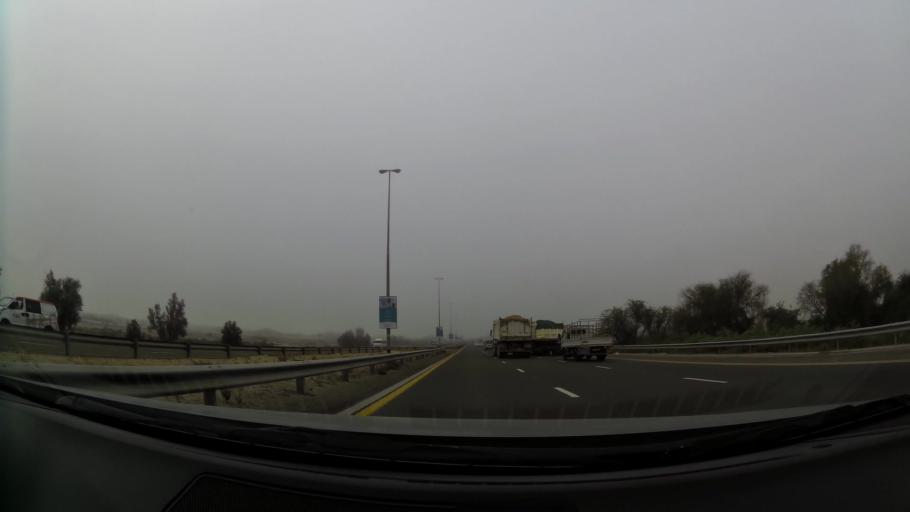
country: AE
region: Dubai
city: Dubai
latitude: 25.1437
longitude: 55.3450
